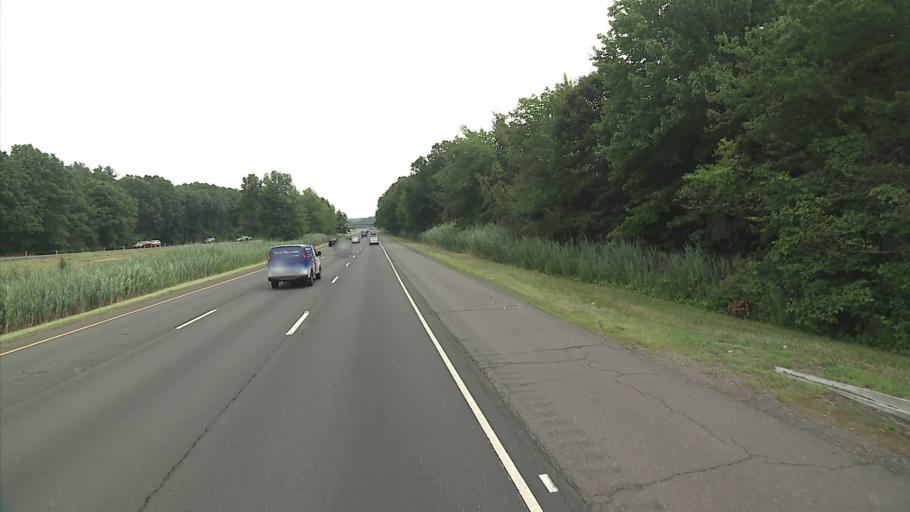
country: US
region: Connecticut
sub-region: Hartford County
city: Plainville
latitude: 41.6464
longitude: -72.8600
